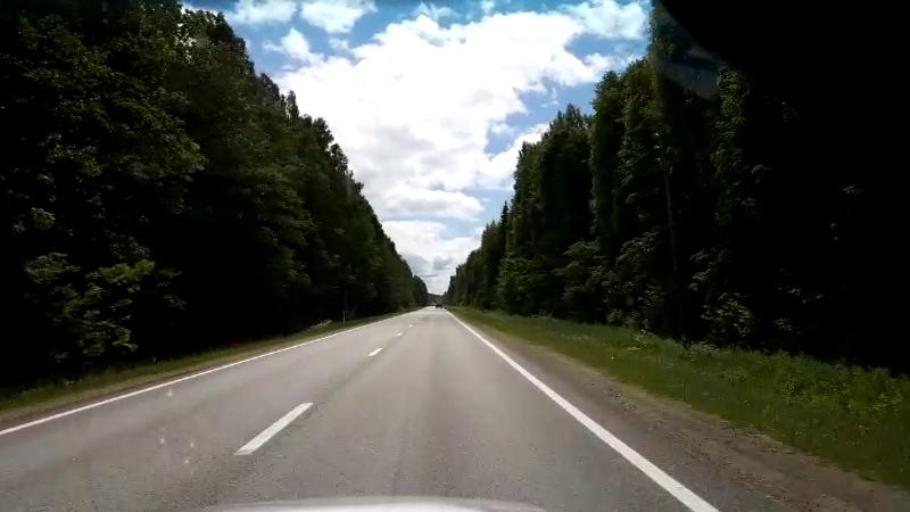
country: LV
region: Salacgrivas
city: Salacgriva
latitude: 57.5874
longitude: 24.4224
